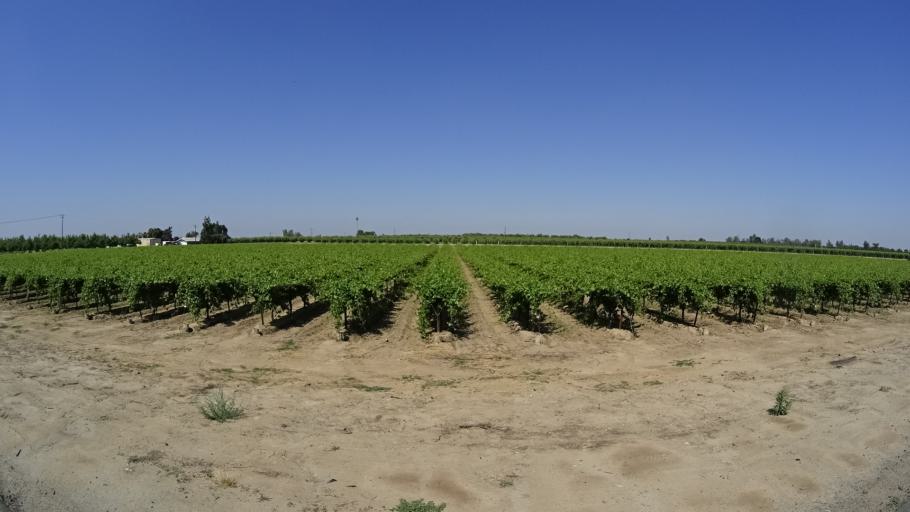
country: US
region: California
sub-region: Fresno County
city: Kingsburg
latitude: 36.4752
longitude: -119.5507
